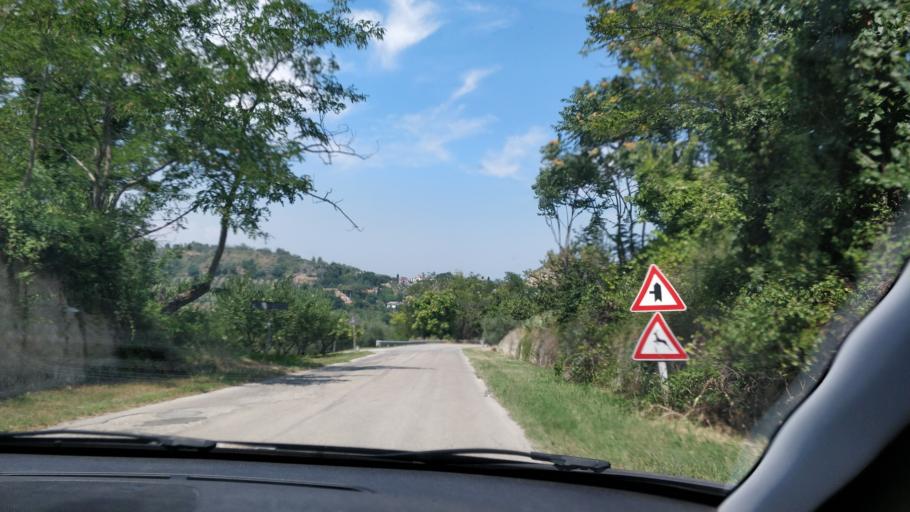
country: IT
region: Abruzzo
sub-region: Provincia di Chieti
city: Torrevecchia
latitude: 42.4011
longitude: 14.2059
